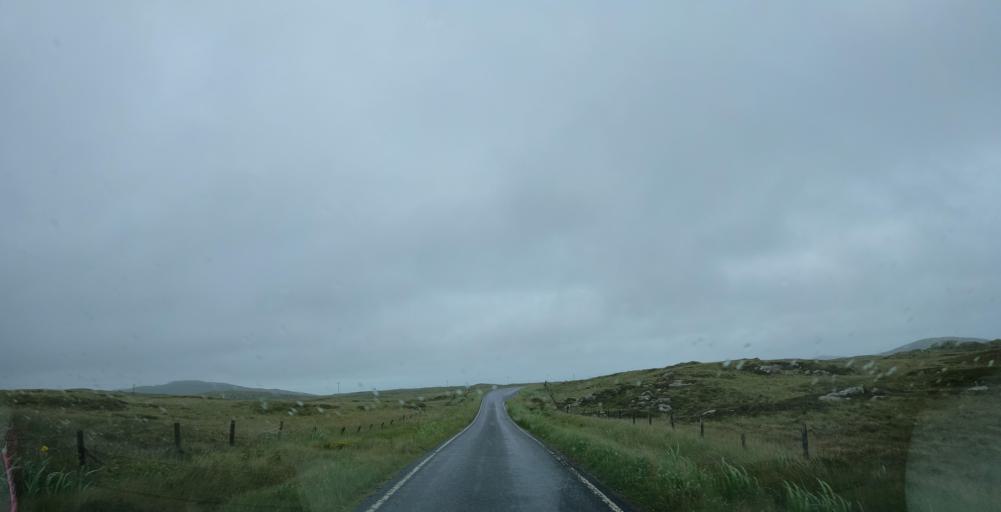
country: GB
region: Scotland
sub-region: Eilean Siar
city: Barra
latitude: 56.9790
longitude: -7.4173
